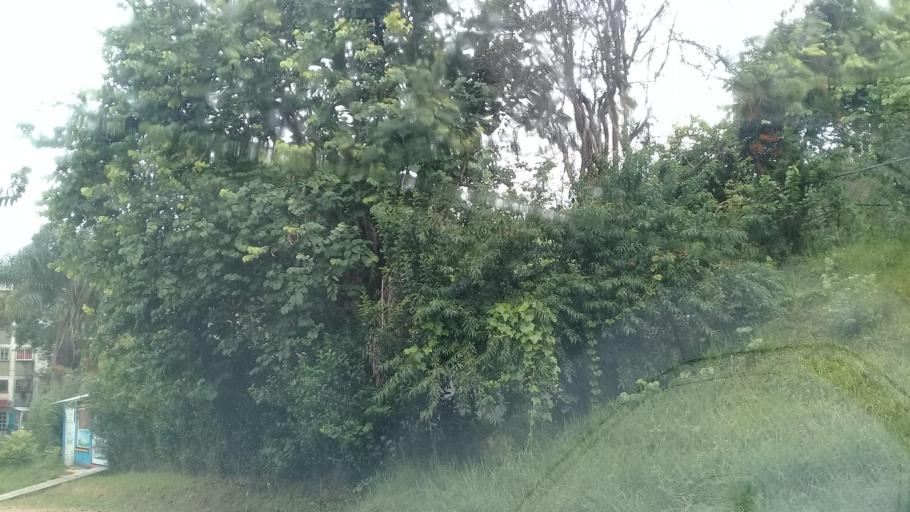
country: MX
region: Veracruz
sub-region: Xalapa
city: Lomas Verdes
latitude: 19.5144
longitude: -96.9027
